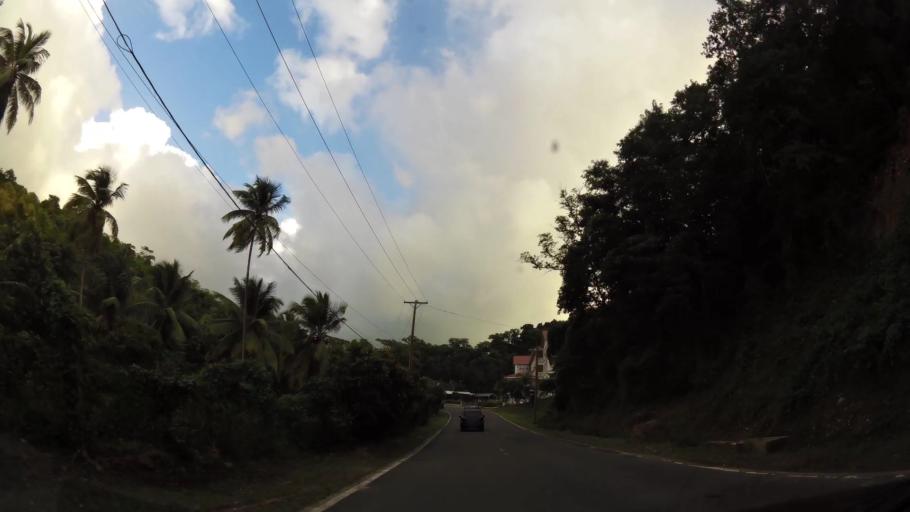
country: DM
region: Saint John
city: Portsmouth
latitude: 15.5443
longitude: -61.4693
